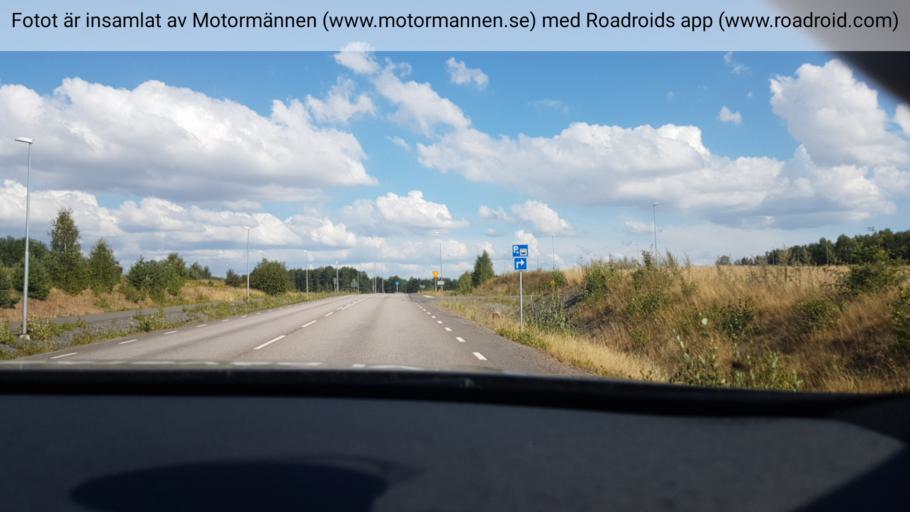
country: SE
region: Vaestra Goetaland
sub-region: Gotene Kommun
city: Kallby
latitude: 58.5011
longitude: 13.3018
